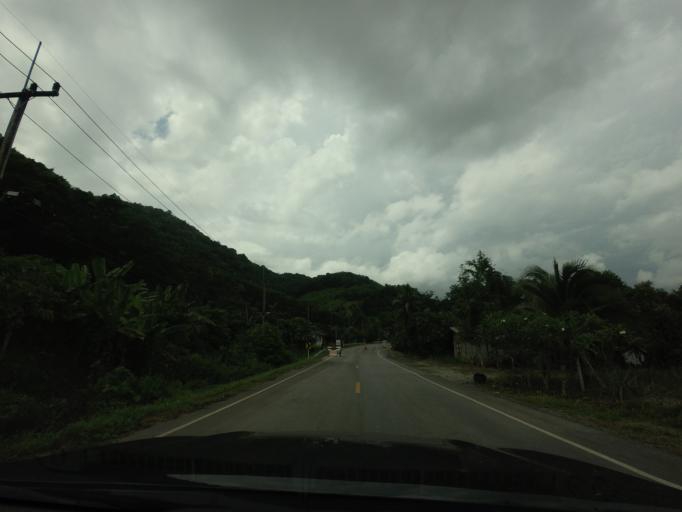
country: TH
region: Loei
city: Pak Chom
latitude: 18.0629
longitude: 101.7936
